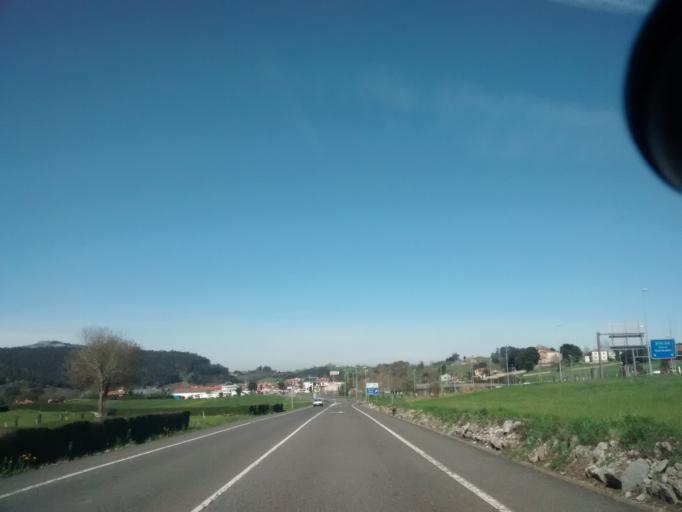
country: ES
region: Cantabria
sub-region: Provincia de Cantabria
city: Entrambasaguas
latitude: 43.3875
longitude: -3.6795
